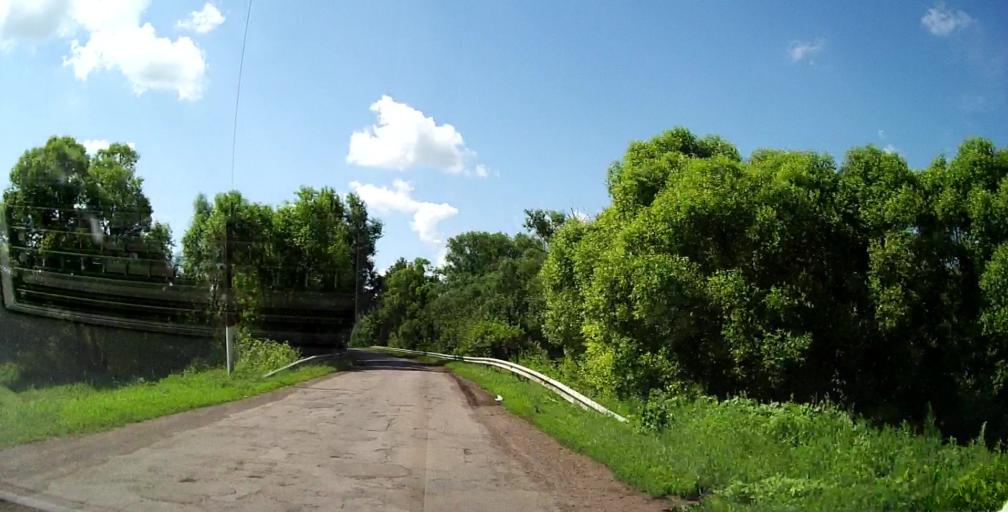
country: RU
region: Lipetsk
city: Chaplygin
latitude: 53.3718
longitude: 39.9165
